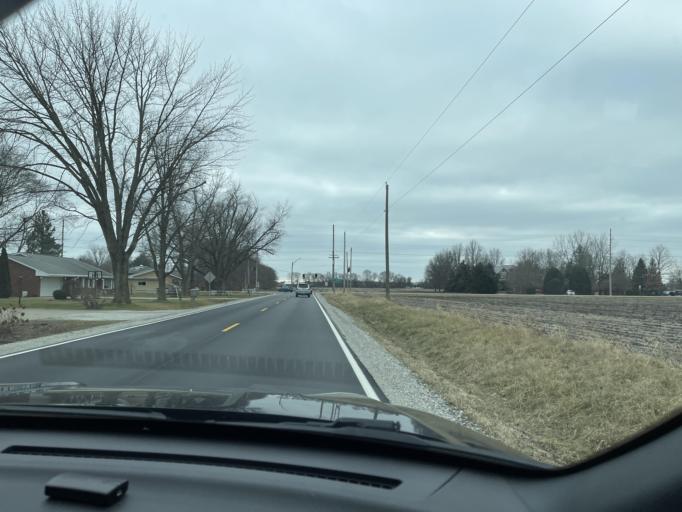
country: US
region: Illinois
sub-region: Sangamon County
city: Leland Grove
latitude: 39.7878
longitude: -89.7391
